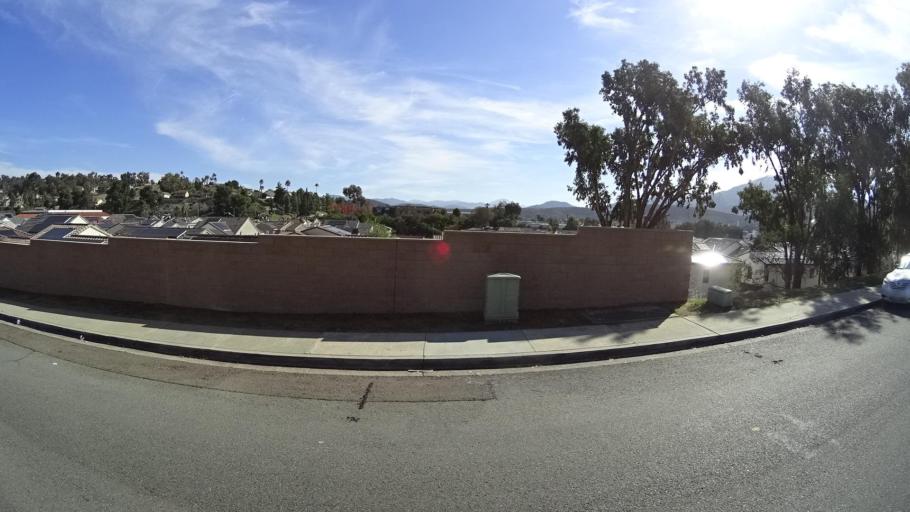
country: US
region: California
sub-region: San Diego County
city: Spring Valley
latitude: 32.7301
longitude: -116.9739
